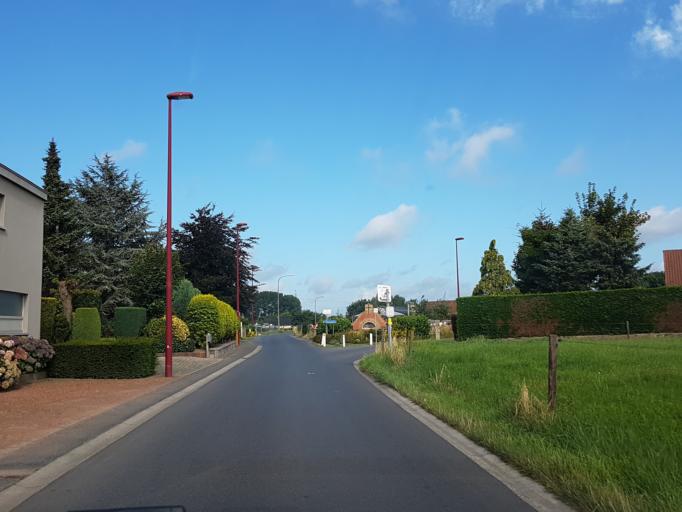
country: BE
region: Flanders
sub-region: Provincie Oost-Vlaanderen
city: Nevele
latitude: 51.0623
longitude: 3.5636
